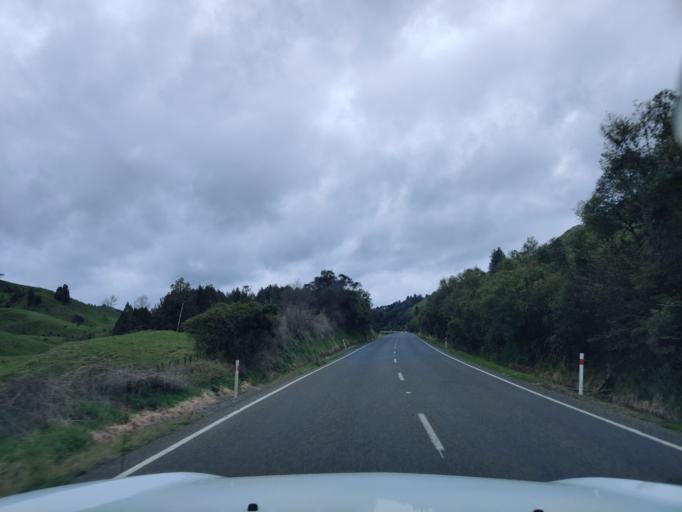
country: NZ
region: Waikato
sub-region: Otorohanga District
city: Otorohanga
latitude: -38.5488
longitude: 175.1865
